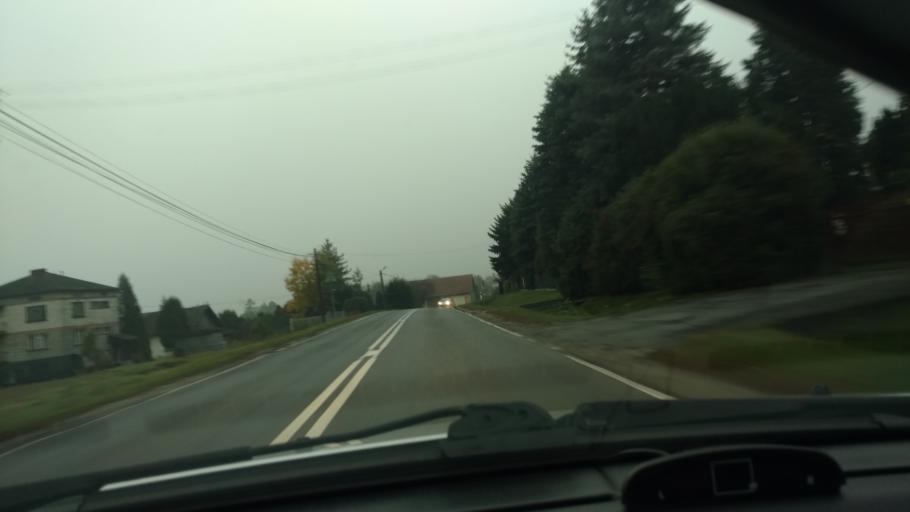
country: PL
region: Subcarpathian Voivodeship
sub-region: Powiat strzyzowski
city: Wisniowa
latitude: 49.8756
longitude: 21.7018
